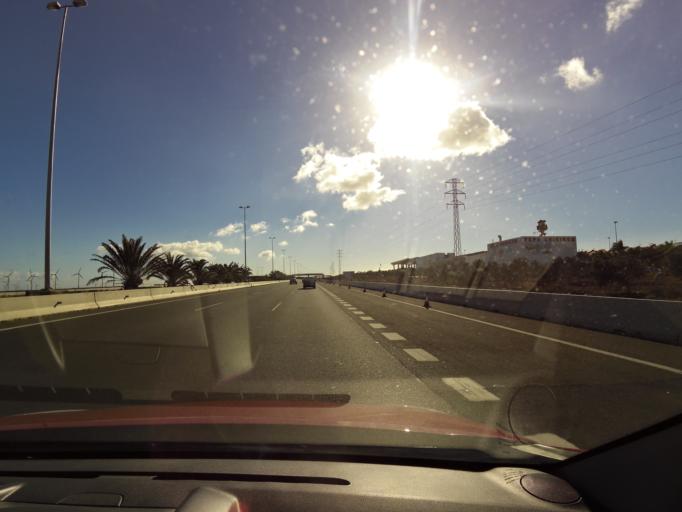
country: ES
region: Canary Islands
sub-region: Provincia de Las Palmas
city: Cruce de Arinaga
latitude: 27.8574
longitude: -15.4282
